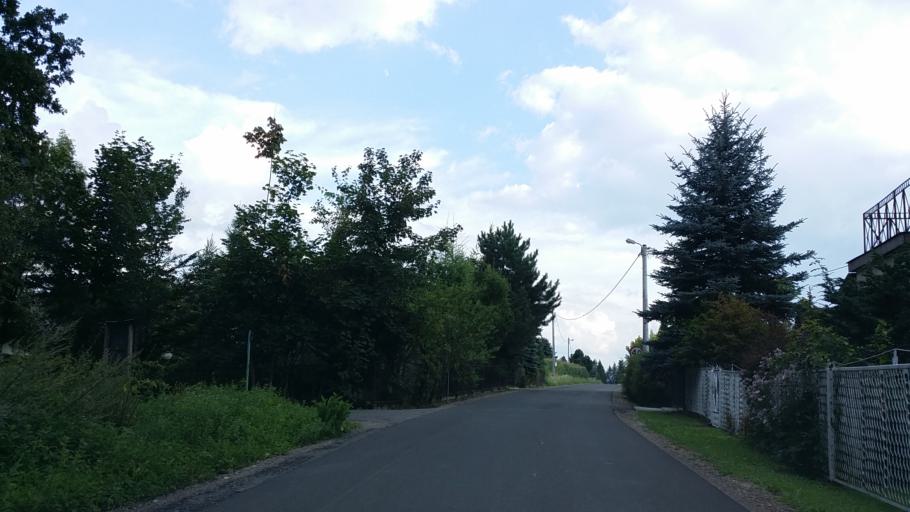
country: PL
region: Lesser Poland Voivodeship
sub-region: Powiat wadowicki
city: Bachowice
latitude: 49.9750
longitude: 19.4786
